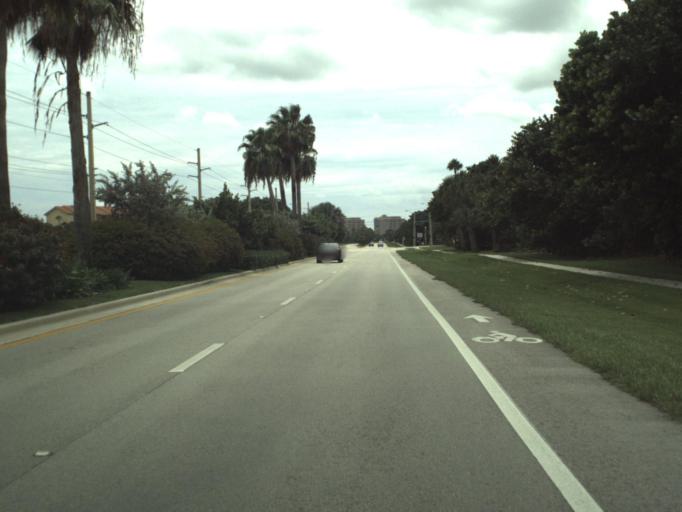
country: US
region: Florida
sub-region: Palm Beach County
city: Juno Beach
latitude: 26.9062
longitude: -80.0667
